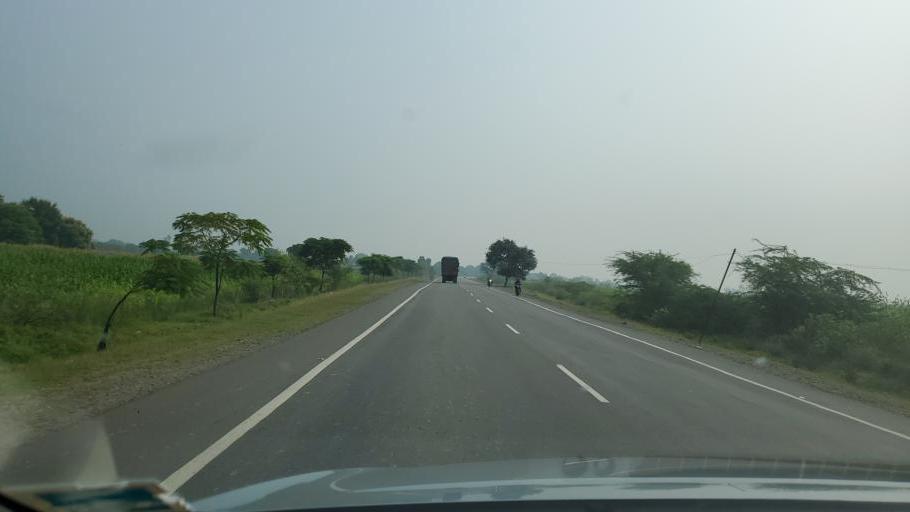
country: IN
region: Tamil Nadu
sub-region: Perambalur
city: Perambalur
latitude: 11.2402
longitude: 79.0022
